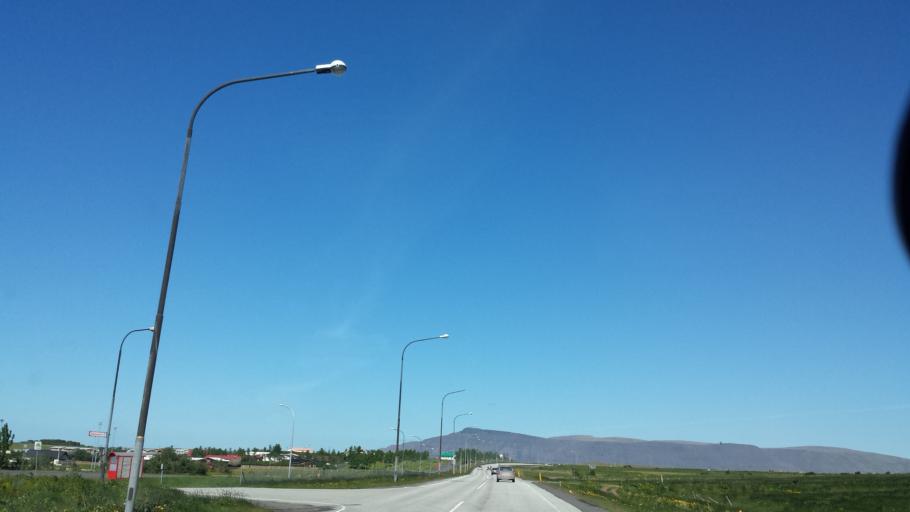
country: IS
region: Capital Region
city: Reykjavik
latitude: 64.2375
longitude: -21.8226
